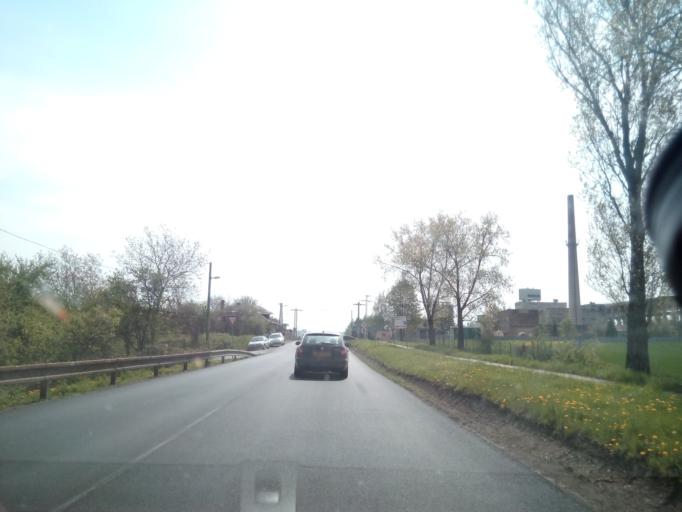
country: SK
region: Presovsky
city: Giraltovce
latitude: 49.0061
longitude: 21.5420
